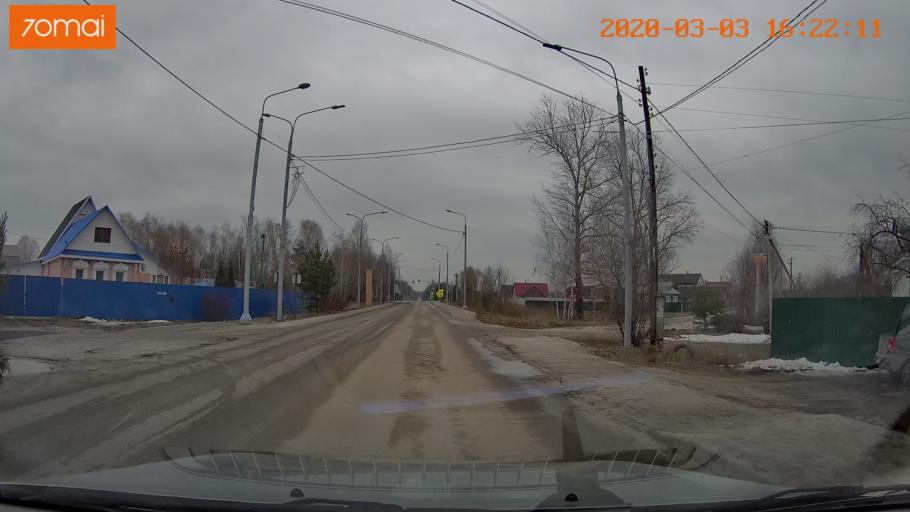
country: RU
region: Moskovskaya
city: Imeni Tsyurupy
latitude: 55.4930
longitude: 38.6473
